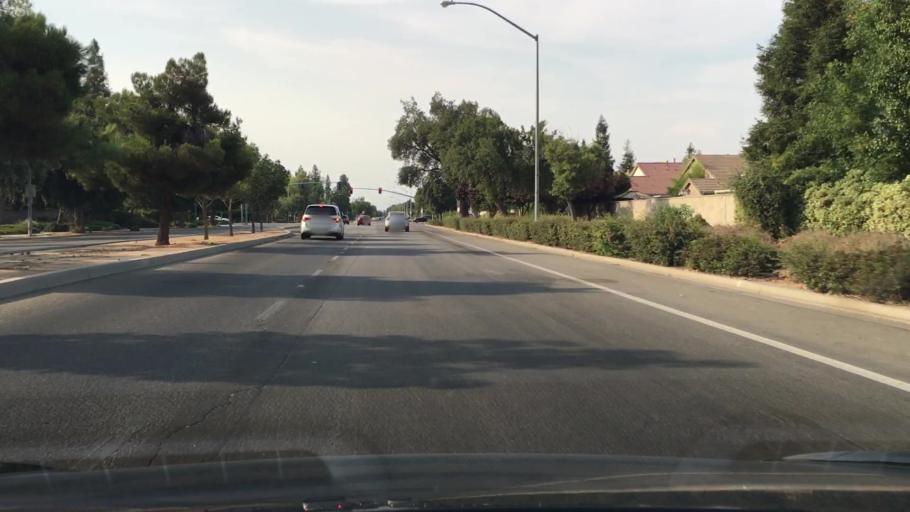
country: US
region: California
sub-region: Fresno County
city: Clovis
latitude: 36.8579
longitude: -119.7387
